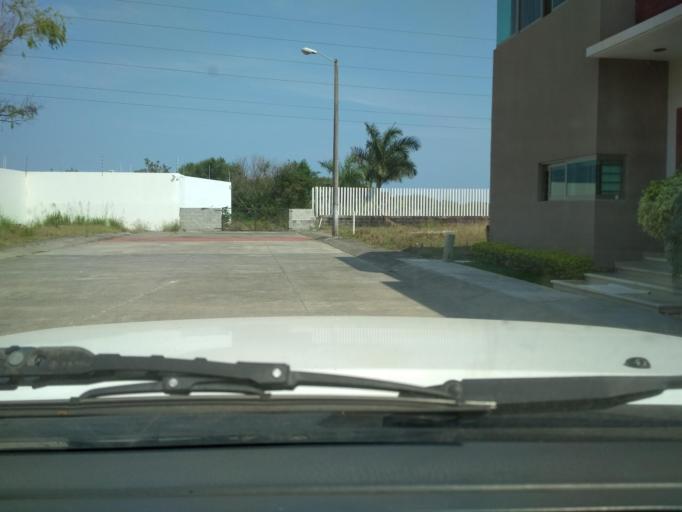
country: MX
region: Veracruz
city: Boca del Rio
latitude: 19.1035
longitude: -96.1211
